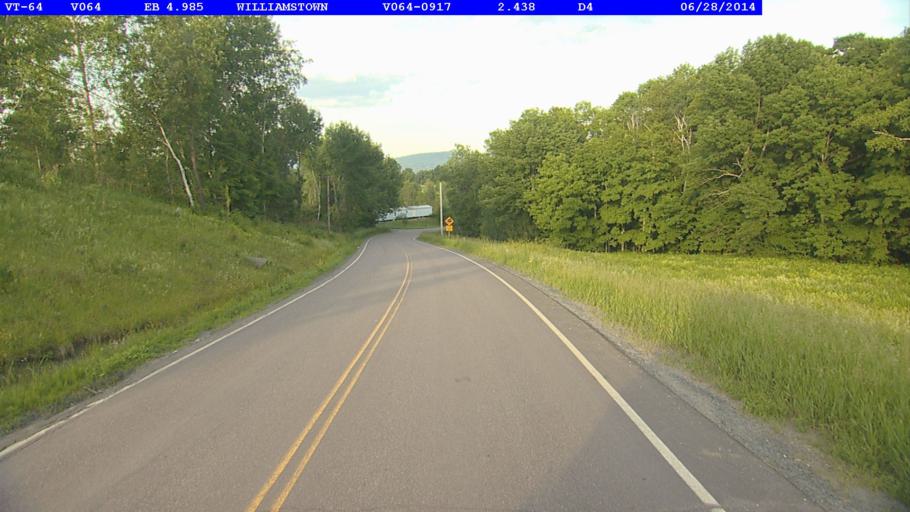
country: US
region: Vermont
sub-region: Orange County
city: Williamstown
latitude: 44.1174
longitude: -72.5719
